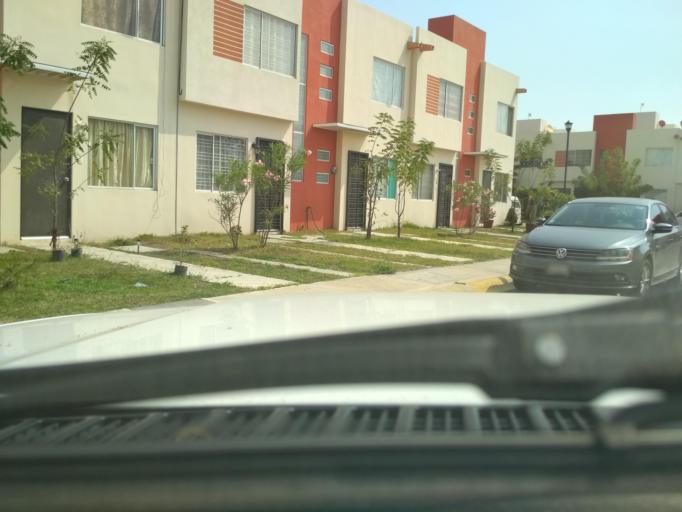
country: MX
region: Veracruz
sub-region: Veracruz
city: Lomas de Rio Medio Cuatro
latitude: 19.1812
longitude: -96.2075
